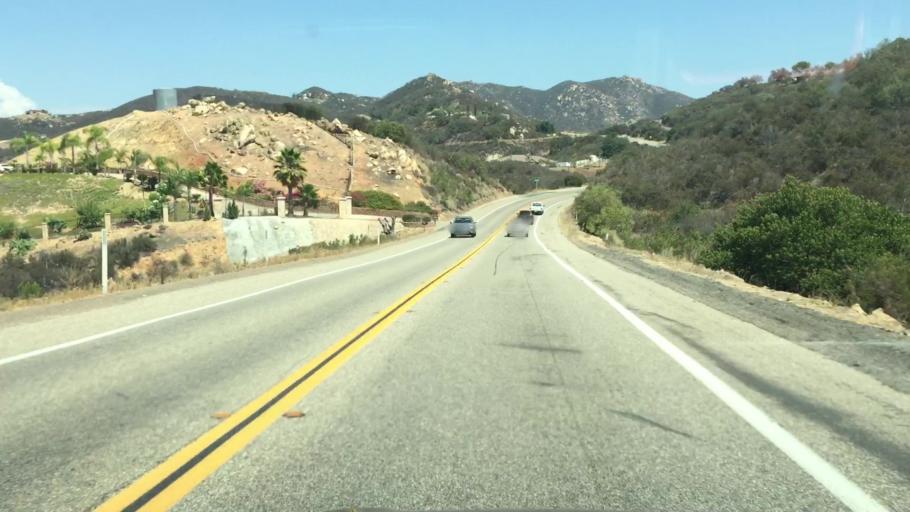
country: US
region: California
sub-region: San Diego County
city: Jamul
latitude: 32.7348
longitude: -116.8275
